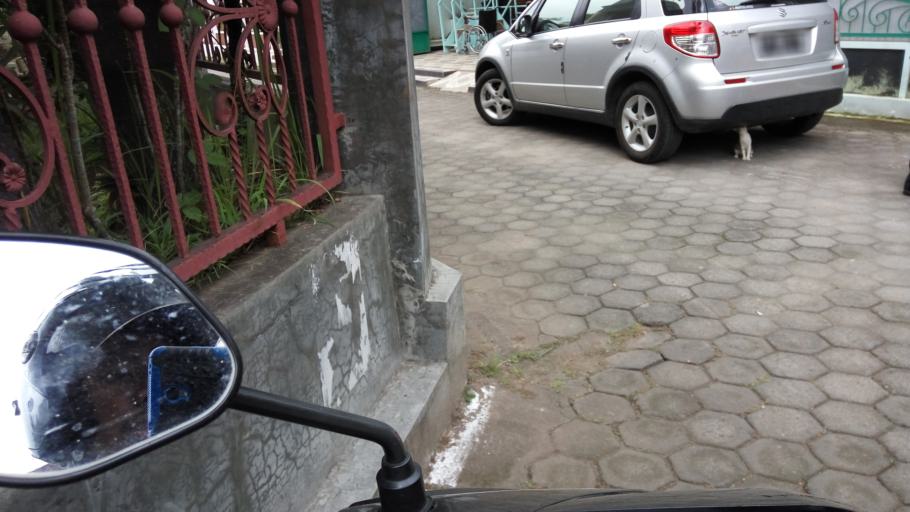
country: ID
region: Central Java
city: Salatiga
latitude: -7.3265
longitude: 110.4945
